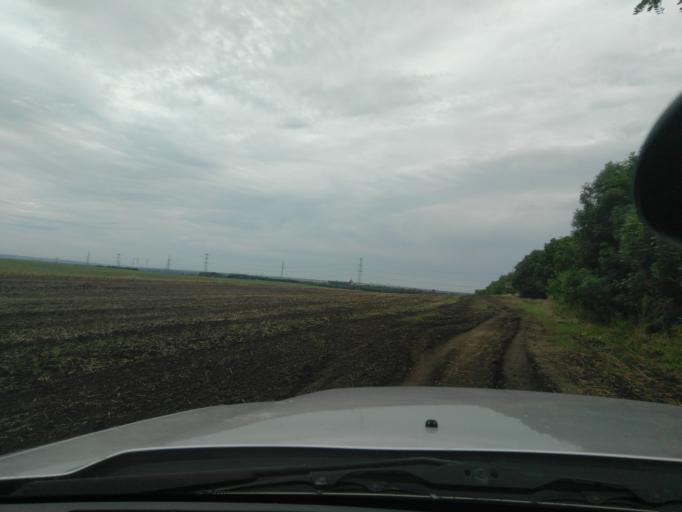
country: HU
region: Fejer
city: Martonvasar
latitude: 47.3569
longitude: 18.7905
